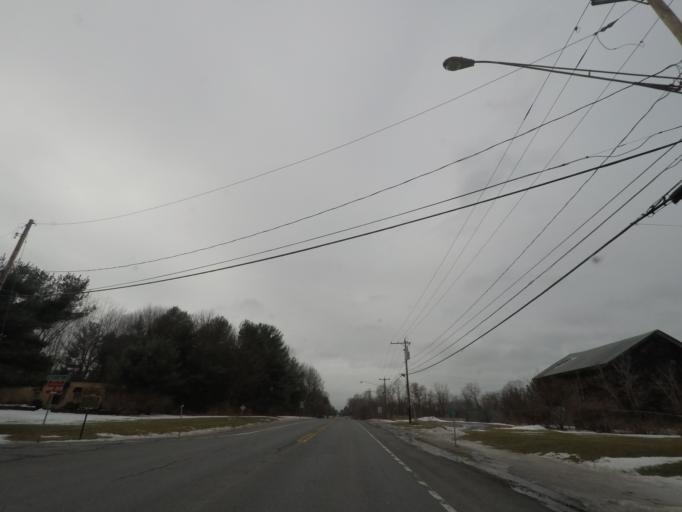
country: US
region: New York
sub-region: Albany County
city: Voorheesville
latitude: 42.7205
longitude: -73.9457
